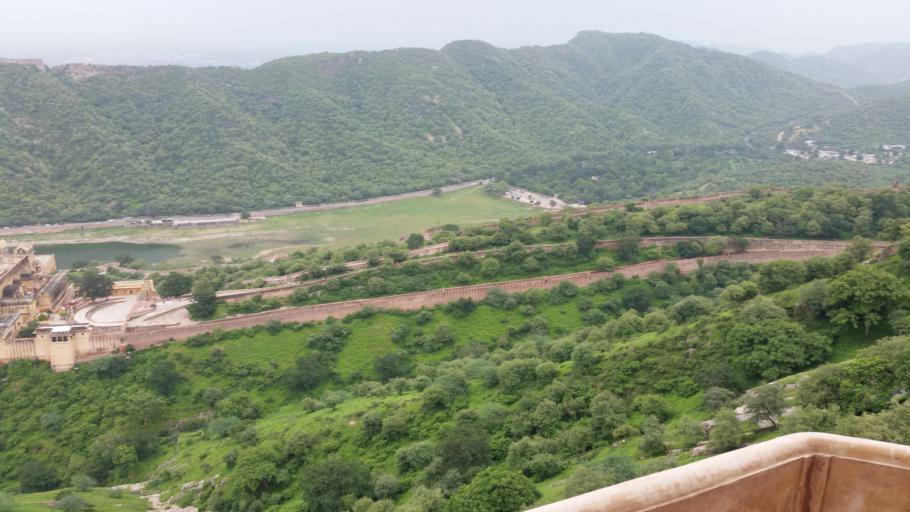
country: IN
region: Rajasthan
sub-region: Jaipur
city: Jaipur
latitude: 26.9858
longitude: 75.8465
